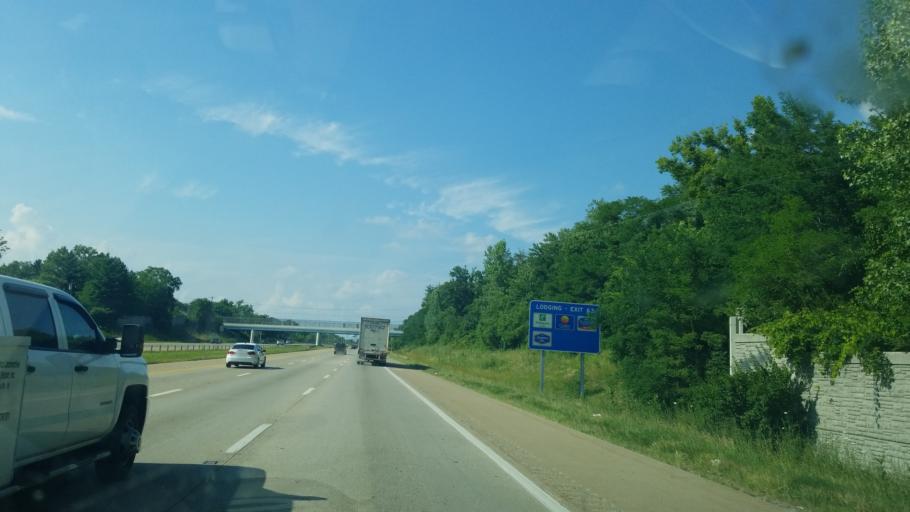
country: US
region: Ohio
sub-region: Clermont County
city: Withamsville
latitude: 39.0824
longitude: -84.2900
